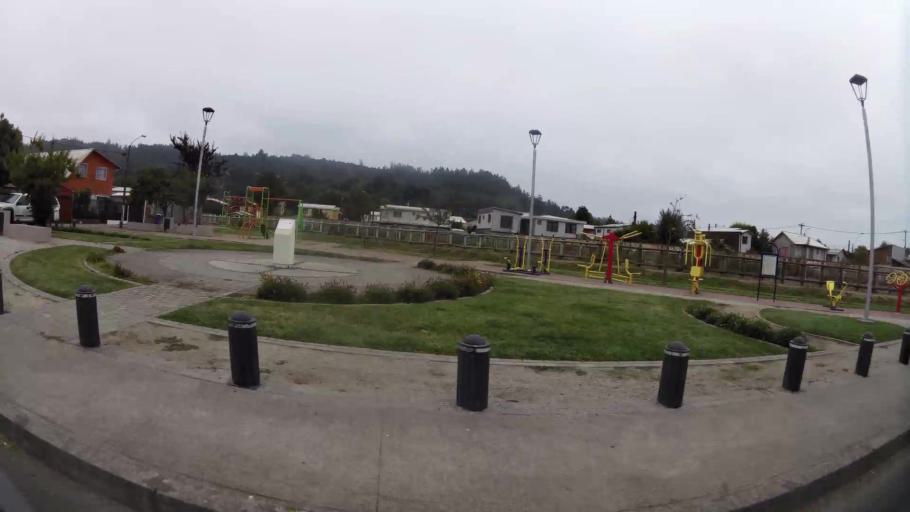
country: CL
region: Biobio
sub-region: Provincia de Concepcion
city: Concepcion
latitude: -36.8290
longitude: -73.0078
